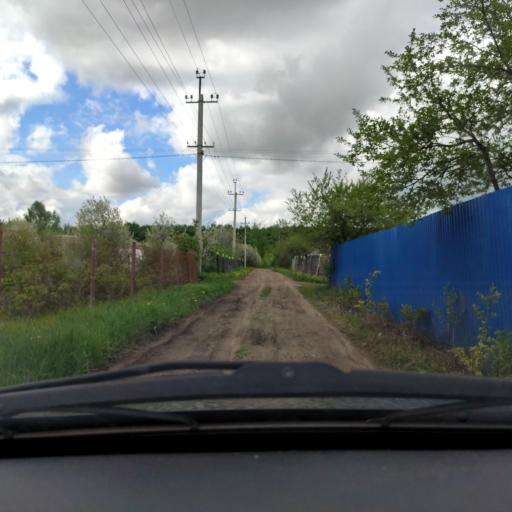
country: RU
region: Bashkortostan
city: Kabakovo
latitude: 54.7095
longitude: 56.1586
